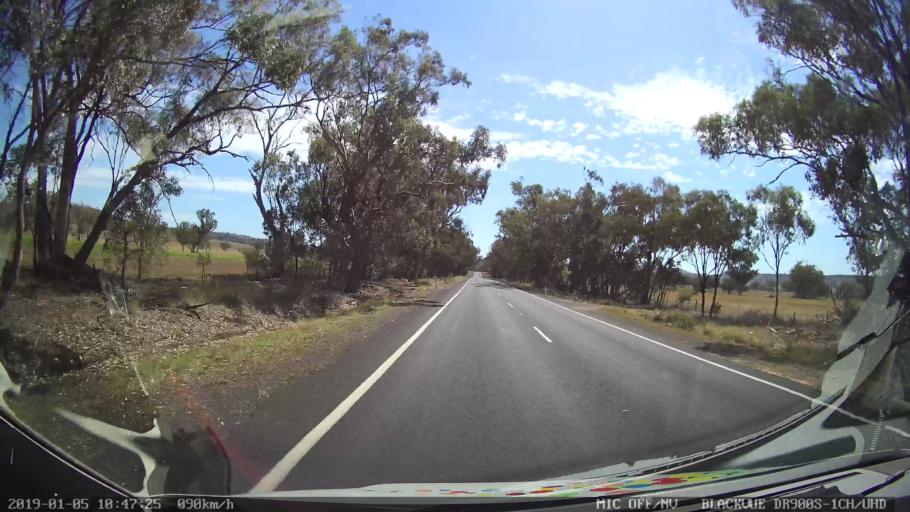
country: AU
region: New South Wales
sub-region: Warrumbungle Shire
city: Coonabarabran
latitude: -31.4451
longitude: 149.0327
